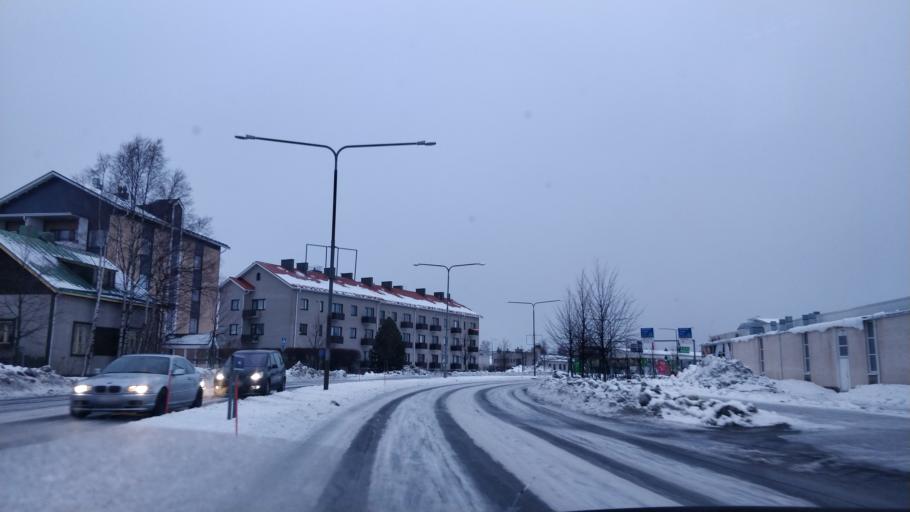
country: FI
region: Lapland
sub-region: Kemi-Tornio
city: Kemi
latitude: 65.7397
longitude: 24.5617
